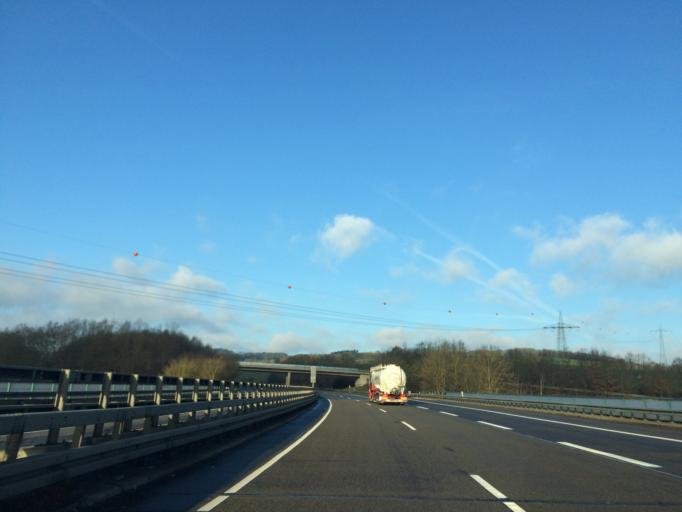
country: DE
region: Hesse
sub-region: Regierungsbezirk Kassel
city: Niederaula
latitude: 50.7755
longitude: 9.5861
